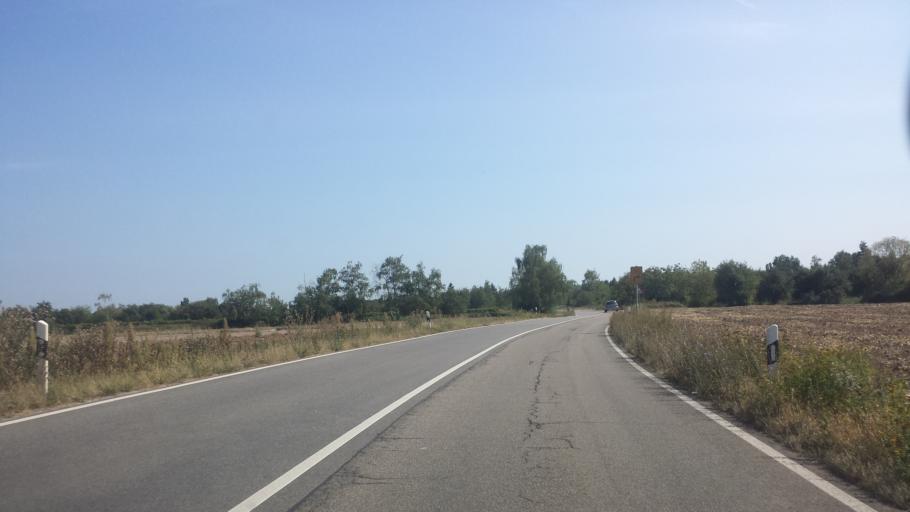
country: DE
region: Rheinland-Pfalz
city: Lachen-Speyerdorf
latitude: 49.3633
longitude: 8.1997
